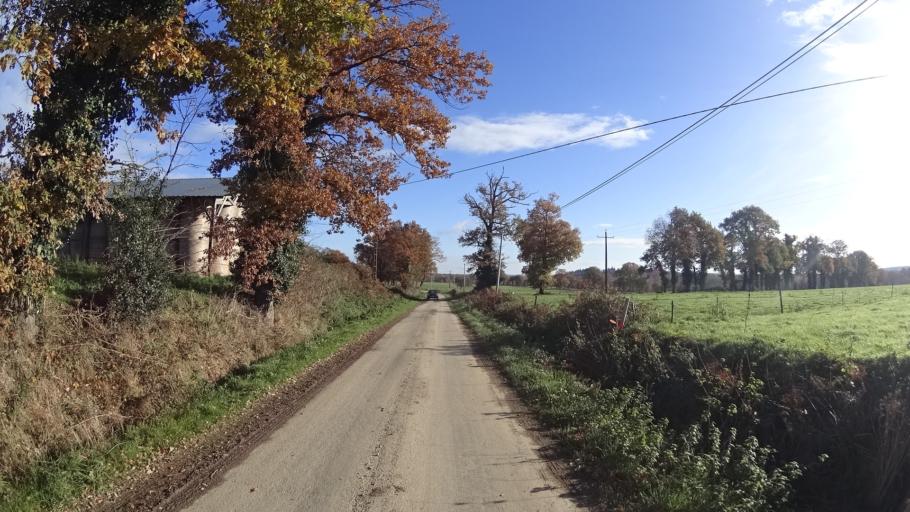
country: FR
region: Brittany
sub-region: Departement du Morbihan
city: Carentoir
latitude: 47.7909
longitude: -2.1713
